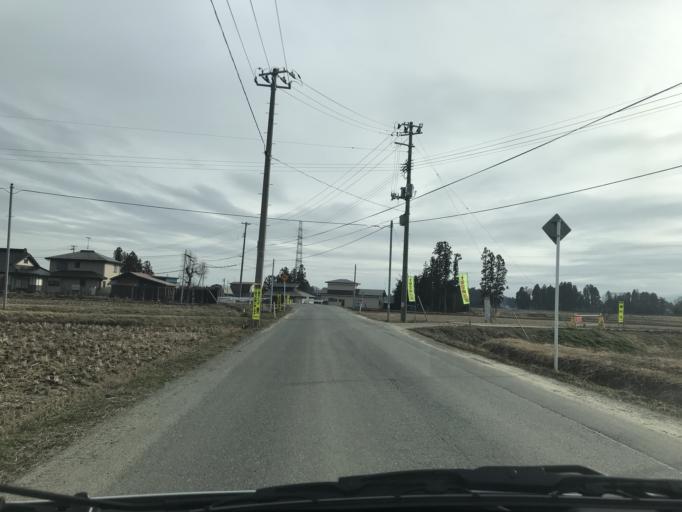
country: JP
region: Iwate
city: Hanamaki
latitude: 39.3406
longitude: 141.0599
